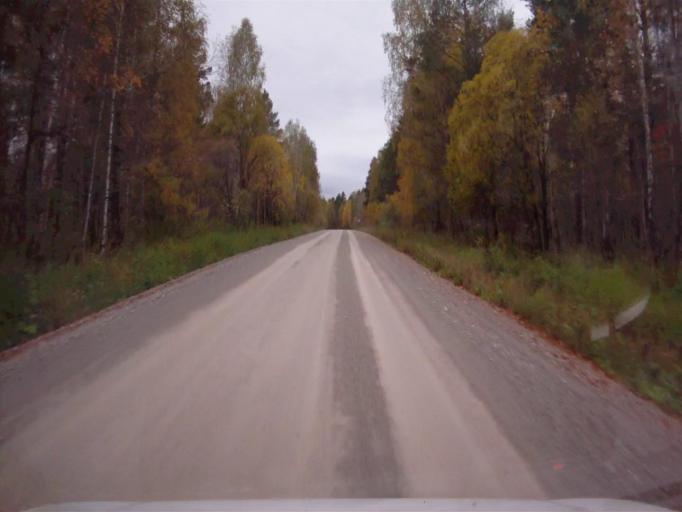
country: RU
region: Chelyabinsk
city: Nyazepetrovsk
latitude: 56.0636
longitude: 59.4430
